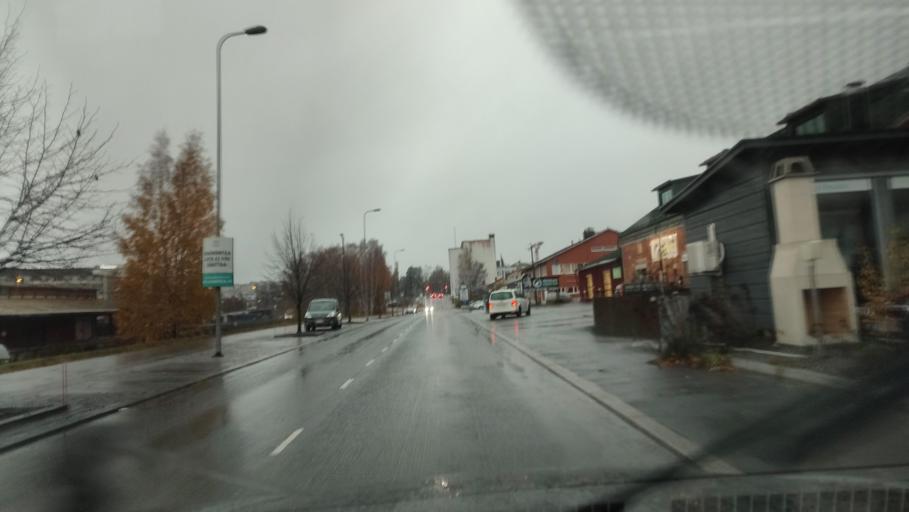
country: FI
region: Ostrobothnia
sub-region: Vaasa
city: Vaasa
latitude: 63.0963
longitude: 21.6299
